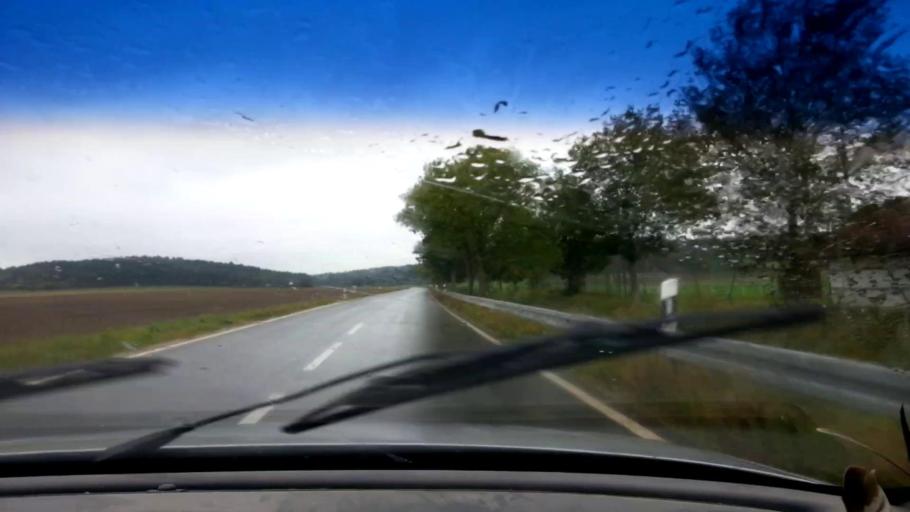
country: DE
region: Bavaria
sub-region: Upper Franconia
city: Konigsfeld
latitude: 49.9434
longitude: 11.1582
